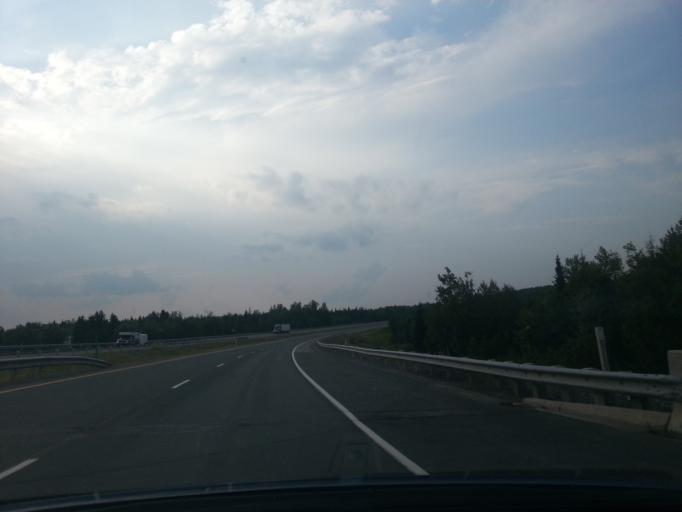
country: CA
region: New Brunswick
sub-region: Madawaska County
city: Saint-Leonard
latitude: 47.1503
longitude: -67.9023
